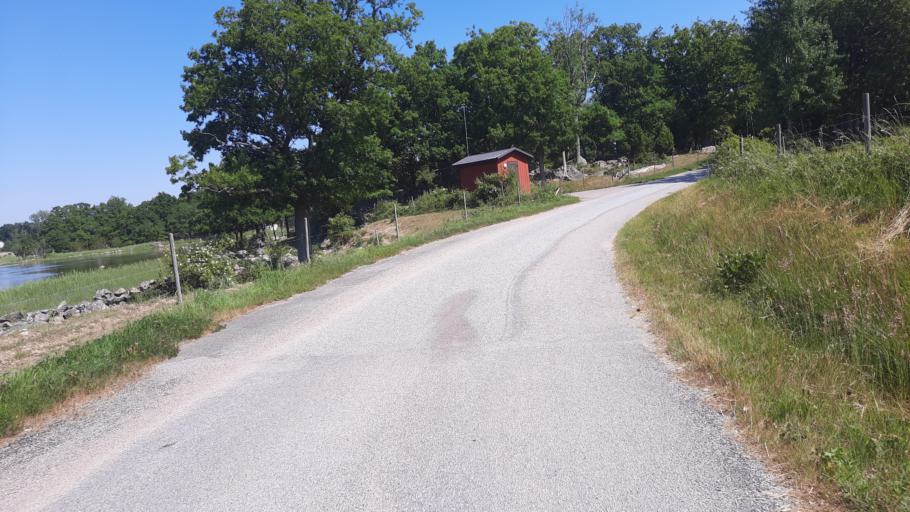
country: SE
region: Blekinge
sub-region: Karlskrona Kommun
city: Jaemjoe
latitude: 56.1577
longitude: 15.7605
